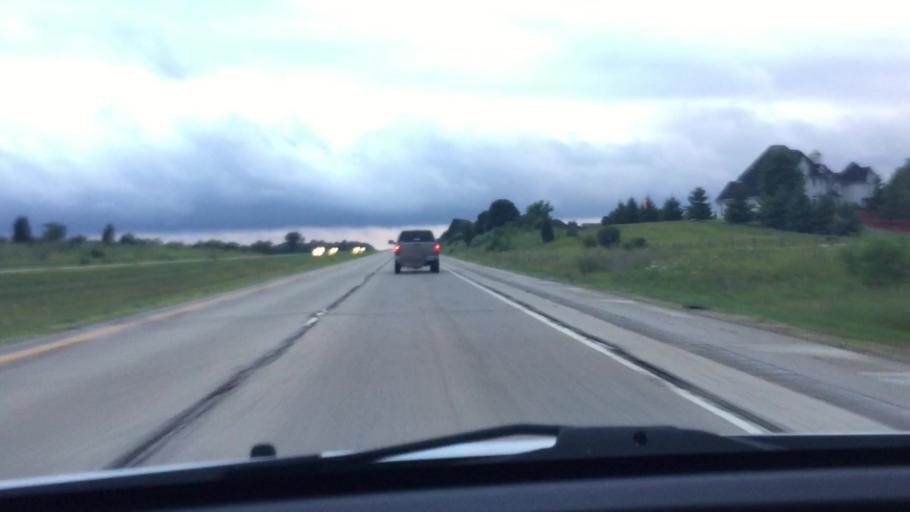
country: US
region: Wisconsin
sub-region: Walworth County
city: Pell Lake
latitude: 42.5692
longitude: -88.3696
